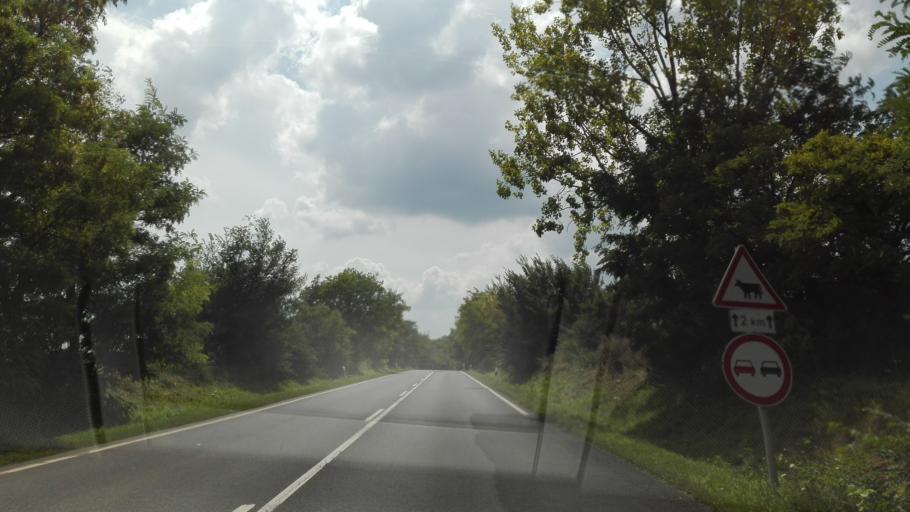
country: HU
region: Fejer
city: Eloszallas
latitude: 46.8181
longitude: 18.7914
